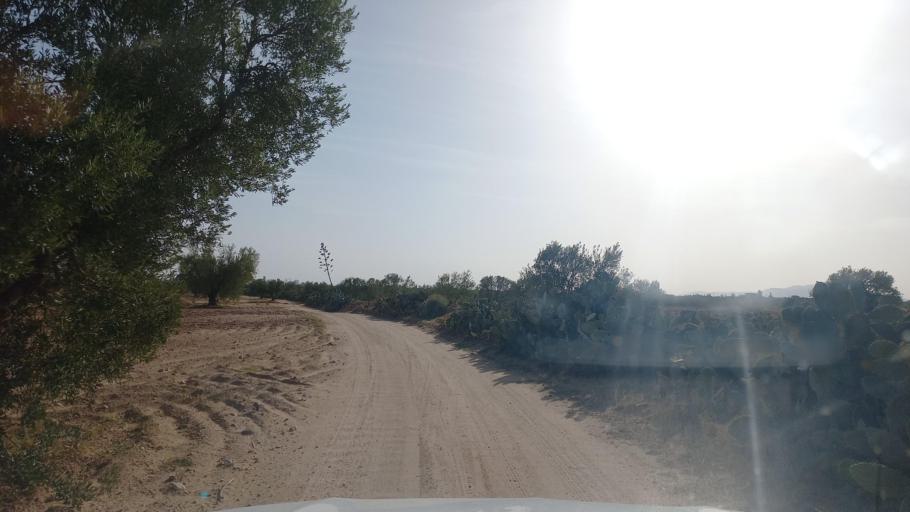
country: TN
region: Al Qasrayn
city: Kasserine
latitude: 35.2281
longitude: 8.9412
